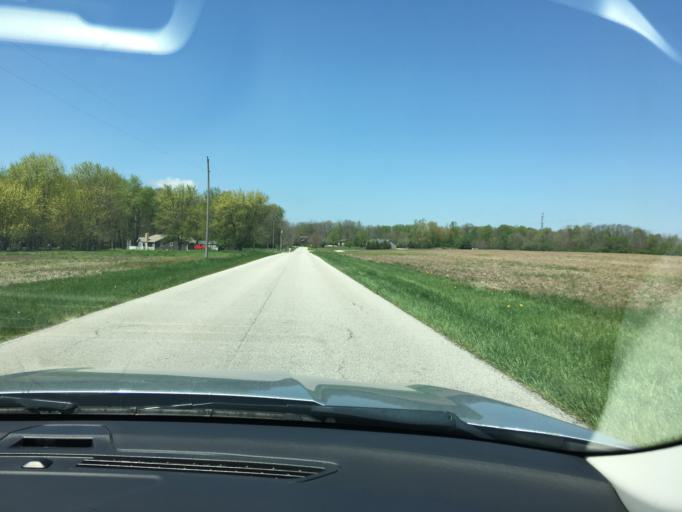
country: US
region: Indiana
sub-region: Tippecanoe County
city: Dayton
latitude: 40.3116
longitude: -86.7414
